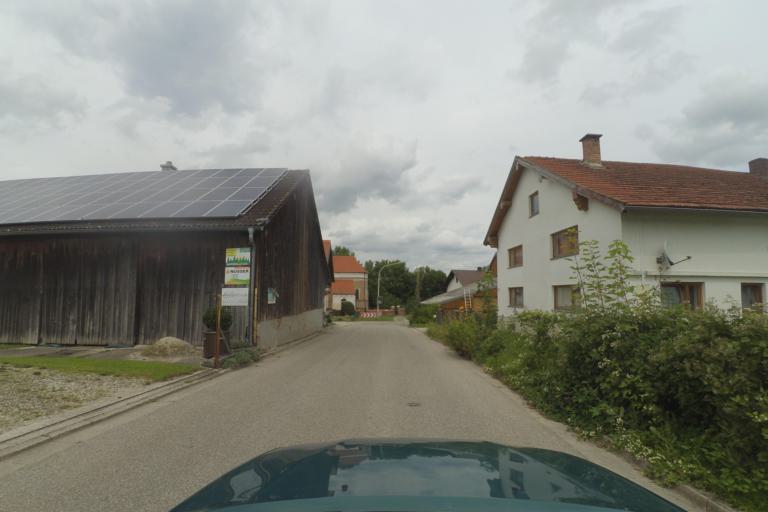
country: DE
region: Bavaria
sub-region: Lower Bavaria
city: Pilsting
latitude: 48.6627
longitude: 12.6474
